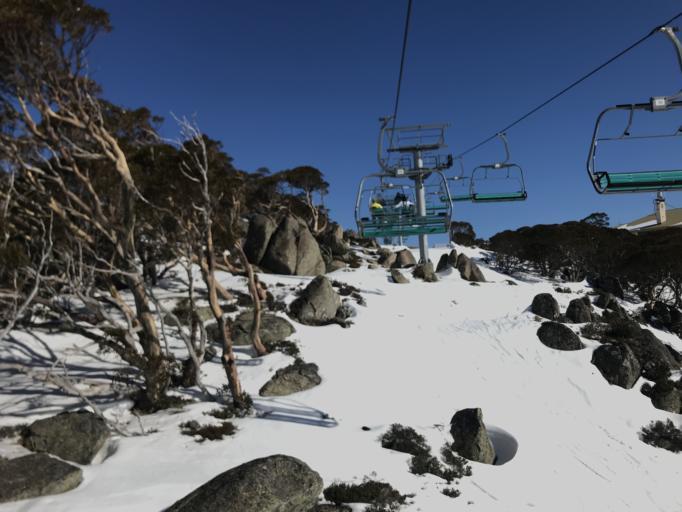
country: AU
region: New South Wales
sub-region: Snowy River
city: Jindabyne
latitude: -36.3855
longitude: 148.3947
